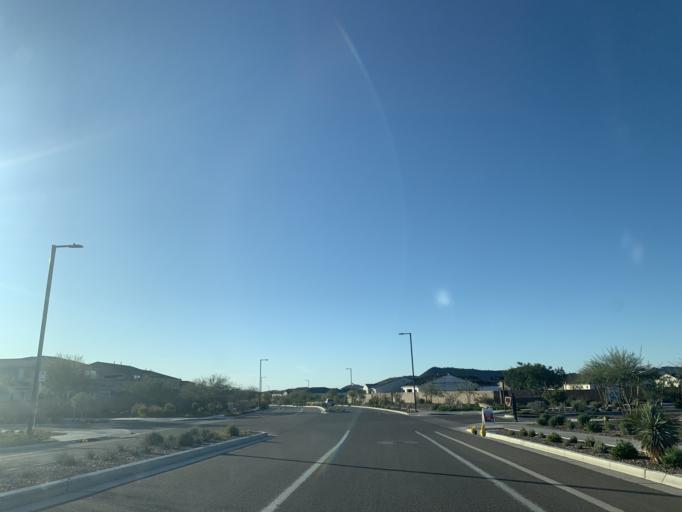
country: US
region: Arizona
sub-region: Maricopa County
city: Cave Creek
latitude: 33.6890
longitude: -112.0150
